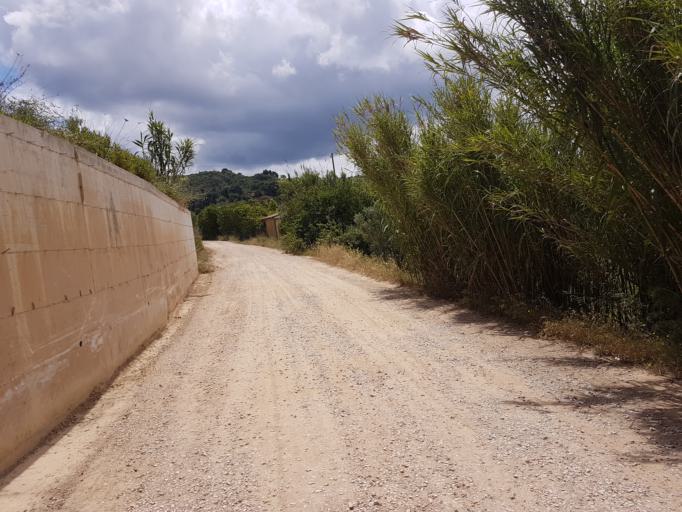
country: IT
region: Tuscany
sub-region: Provincia di Livorno
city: Portoferraio
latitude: 42.7901
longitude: 10.3515
